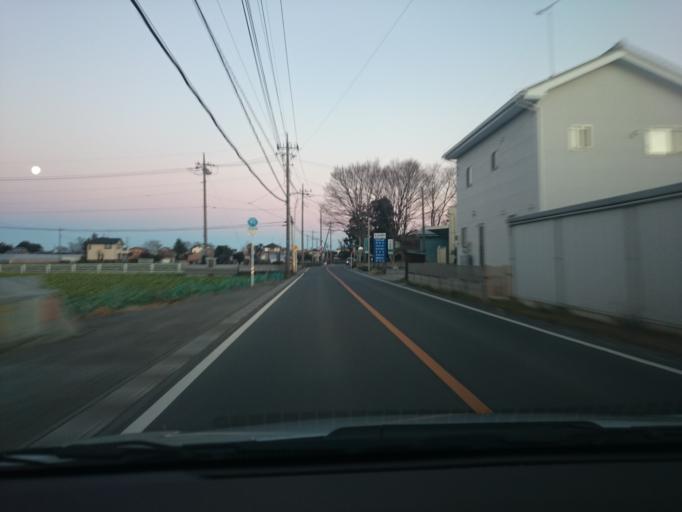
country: JP
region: Saitama
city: Fukayacho
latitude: 36.2295
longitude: 139.2977
